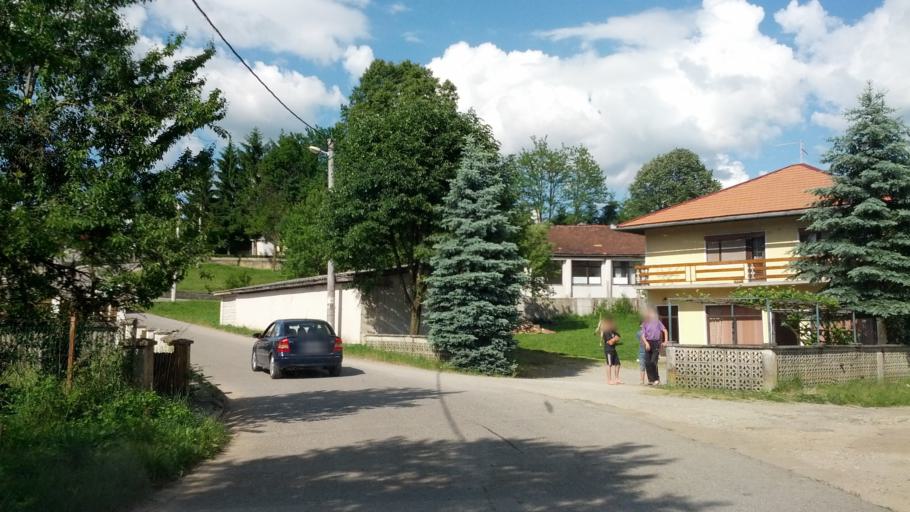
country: BA
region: Federation of Bosnia and Herzegovina
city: Ostrozac
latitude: 44.9202
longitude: 15.9530
